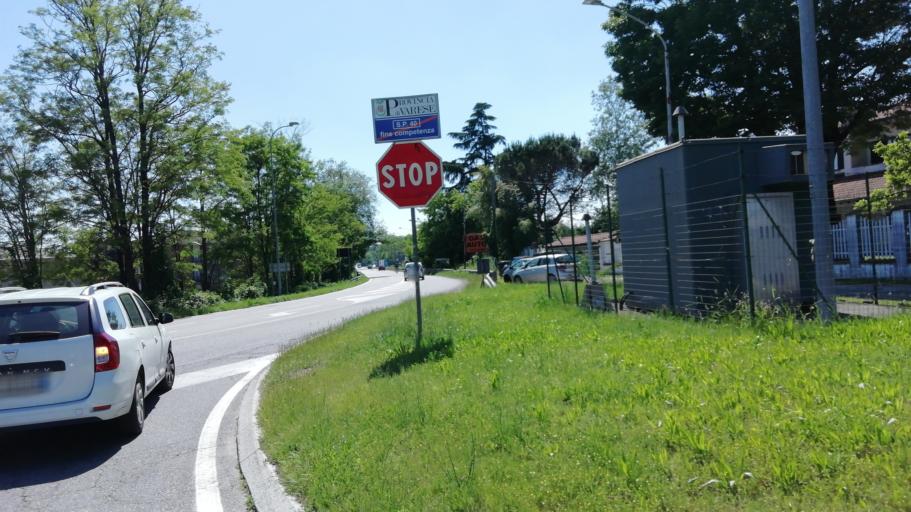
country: IT
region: Lombardy
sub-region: Provincia di Varese
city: Lonate Pozzolo
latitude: 45.5940
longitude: 8.7409
